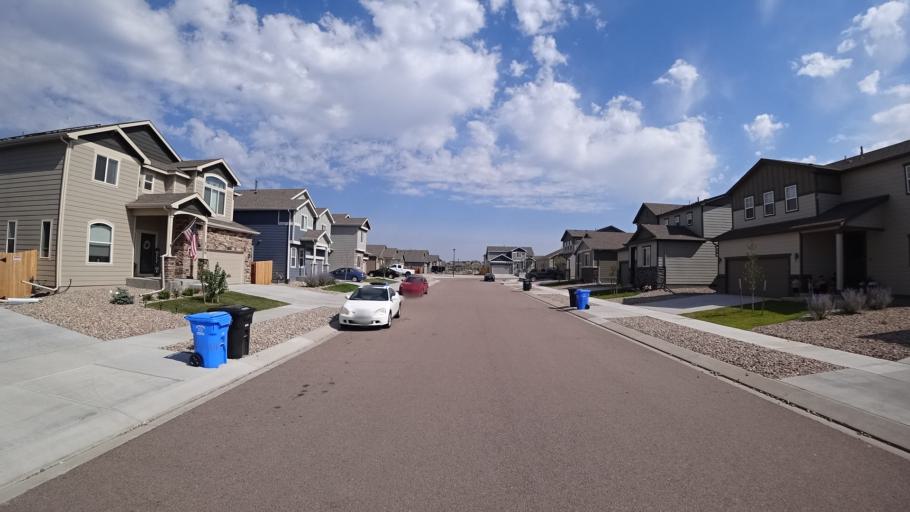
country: US
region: Colorado
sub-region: El Paso County
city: Cimarron Hills
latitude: 38.9200
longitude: -104.6819
